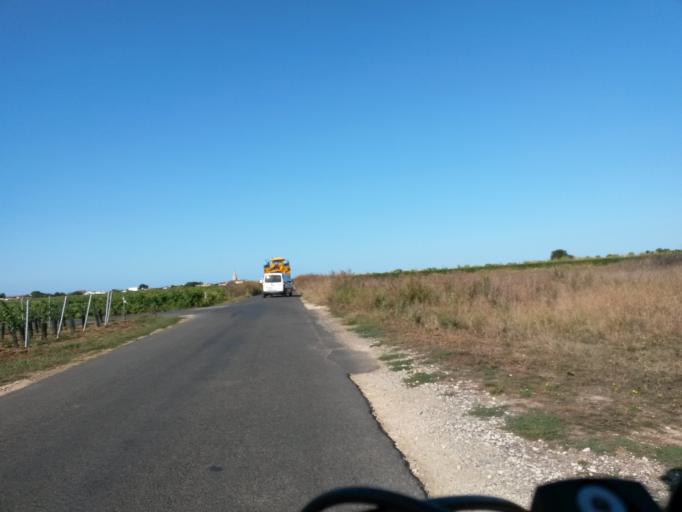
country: FR
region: Poitou-Charentes
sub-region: Departement de la Charente-Maritime
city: Sainte-Marie-de-Re
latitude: 46.1527
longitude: -1.2977
